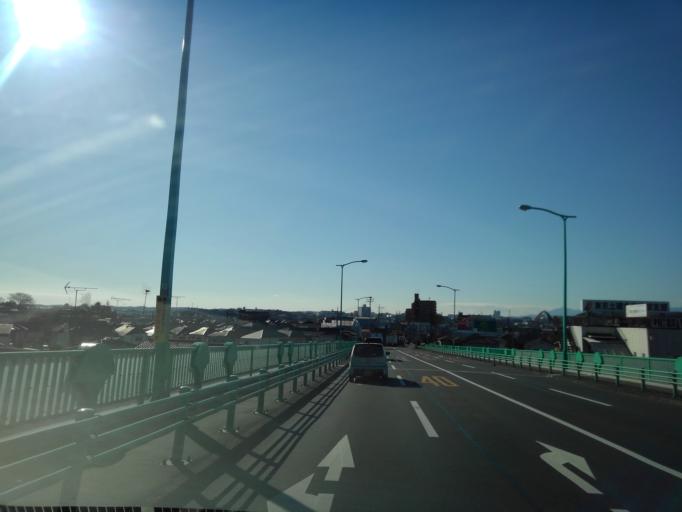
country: JP
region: Tokyo
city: Hino
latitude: 35.7008
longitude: 139.3773
